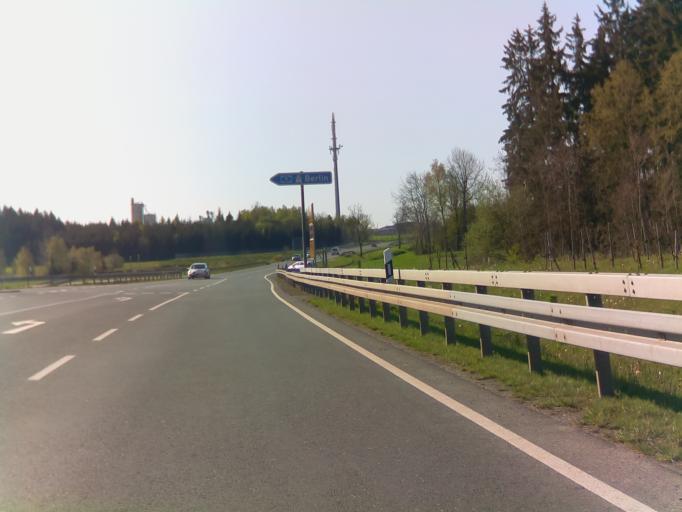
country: DE
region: Thuringia
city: Dittersdorf
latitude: 50.6566
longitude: 11.8138
